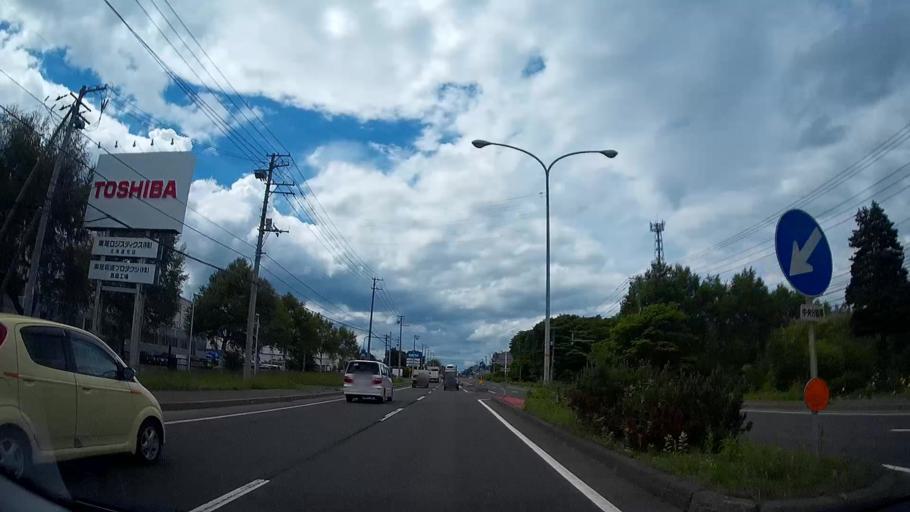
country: JP
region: Hokkaido
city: Chitose
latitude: 42.8630
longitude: 141.5980
